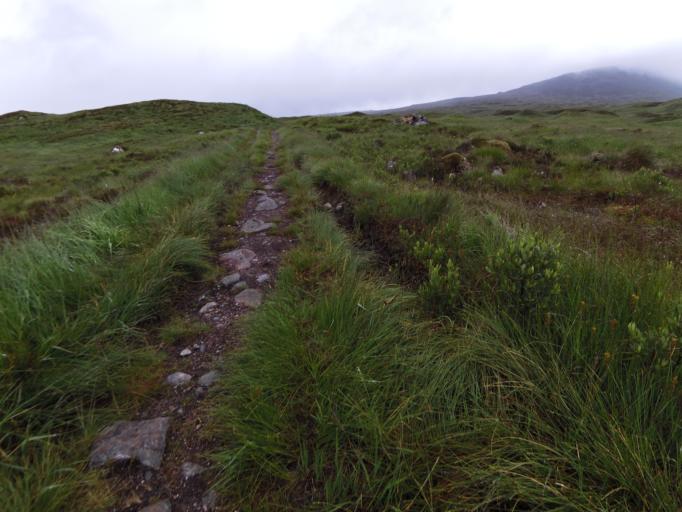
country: GB
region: Scotland
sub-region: Highland
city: Spean Bridge
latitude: 56.7673
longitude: -4.7032
